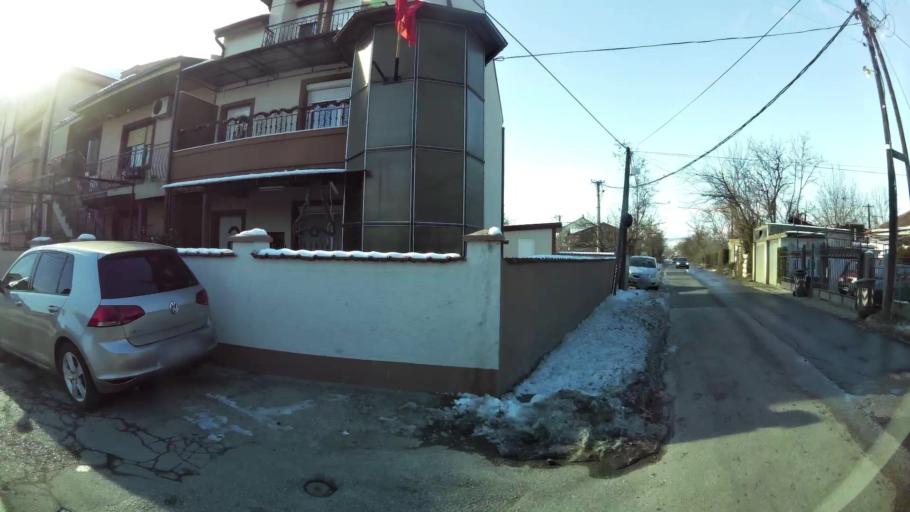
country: MK
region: Saraj
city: Saraj
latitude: 42.0101
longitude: 21.3534
